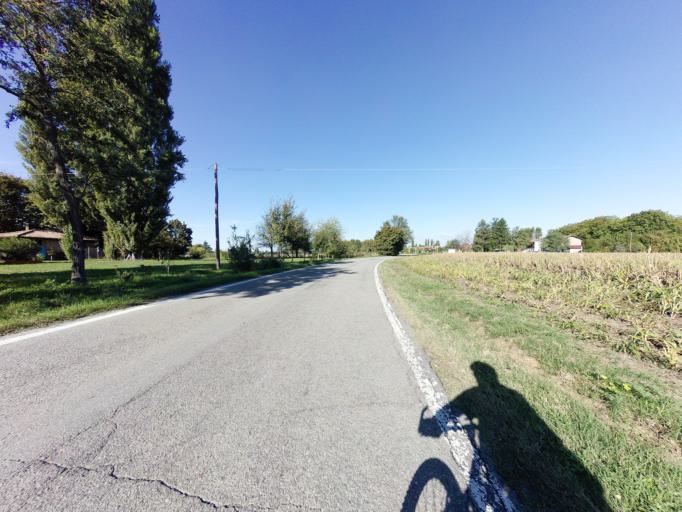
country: IT
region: Emilia-Romagna
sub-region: Provincia di Bologna
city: Progresso
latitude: 44.5667
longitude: 11.3892
